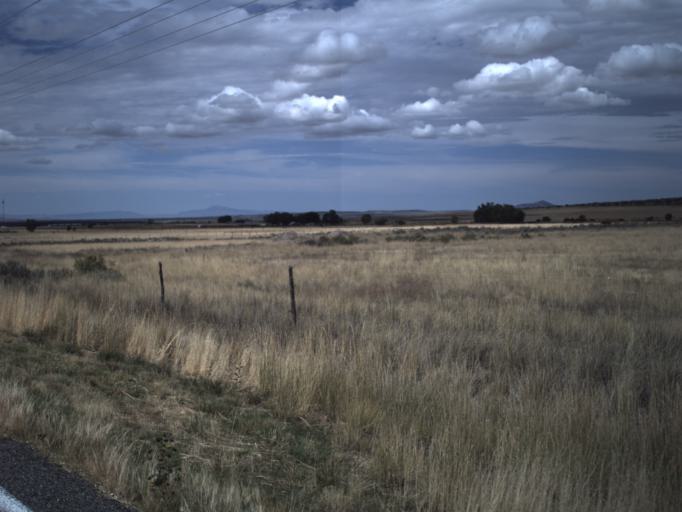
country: US
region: Utah
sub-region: Millard County
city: Fillmore
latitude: 38.9792
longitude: -112.3880
